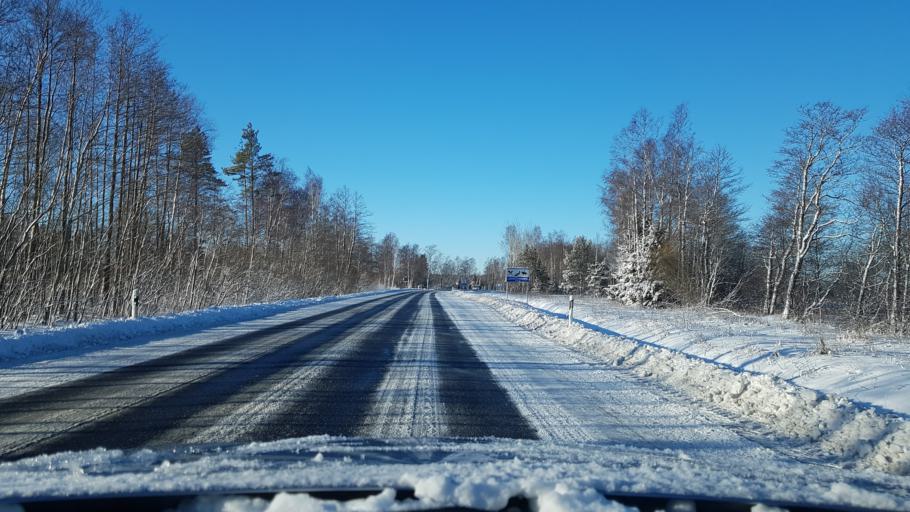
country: EE
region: Hiiumaa
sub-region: Kaerdla linn
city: Kardla
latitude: 58.9881
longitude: 22.7761
